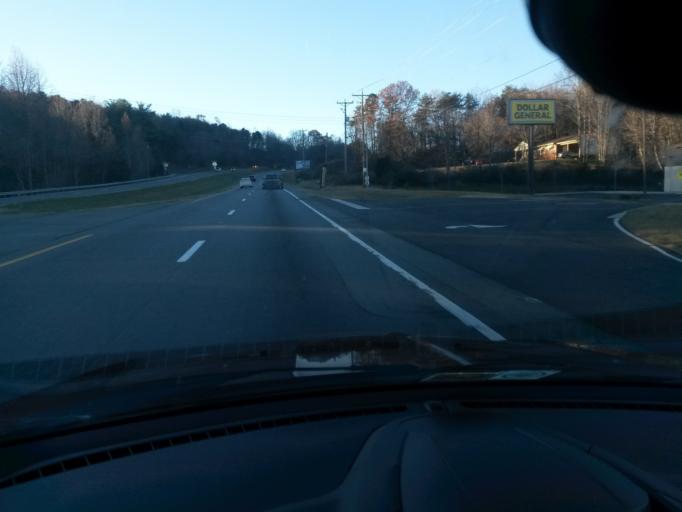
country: US
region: Virginia
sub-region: Henry County
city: Stanleytown
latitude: 36.8354
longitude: -79.9197
